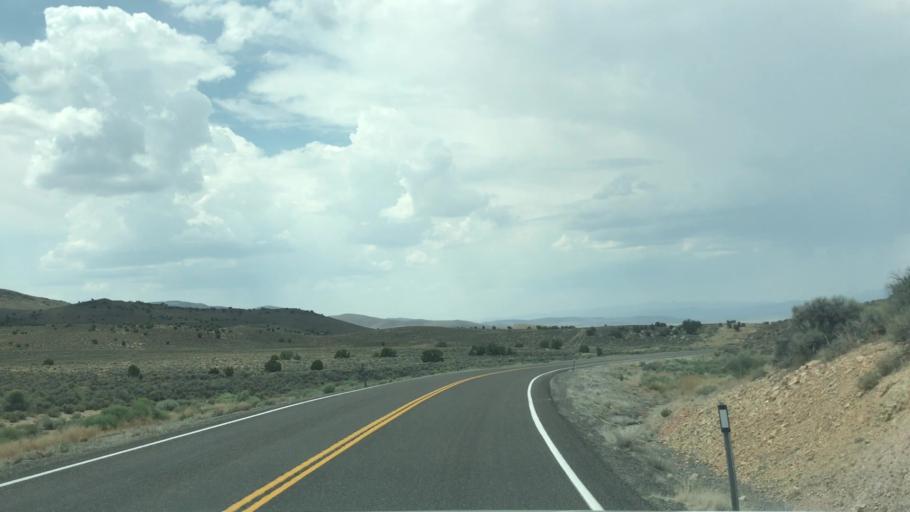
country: US
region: Nevada
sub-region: Eureka County
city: Eureka
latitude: 39.4009
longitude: -115.7044
